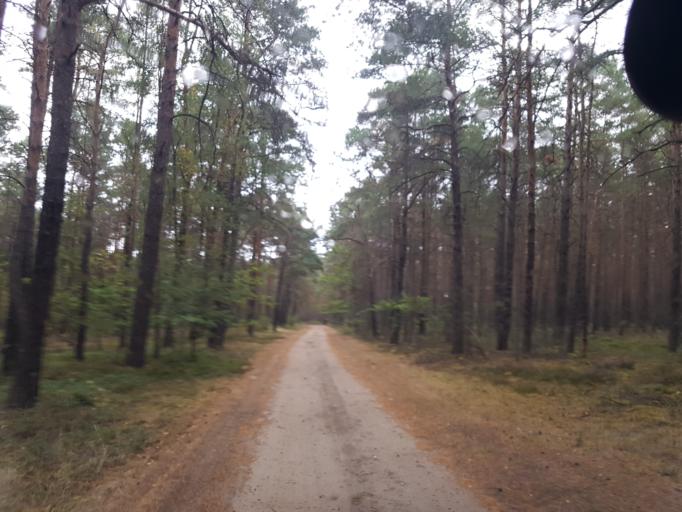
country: DE
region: Brandenburg
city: Sallgast
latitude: 51.6120
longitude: 13.7786
